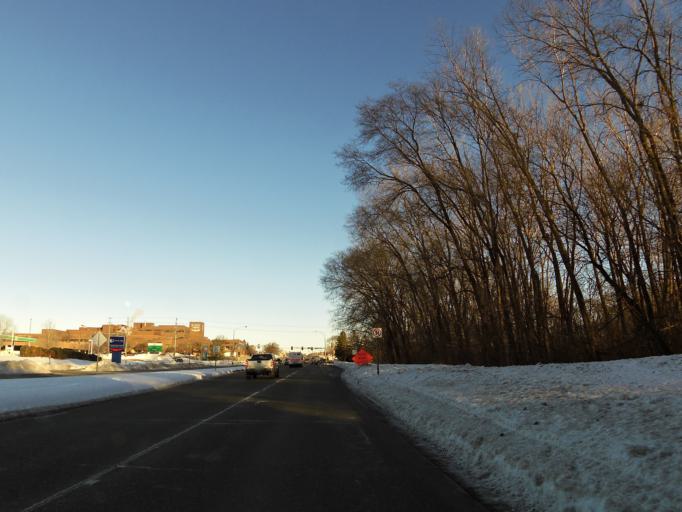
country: US
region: Minnesota
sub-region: Ramsey County
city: Vadnais Heights
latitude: 45.0280
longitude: -93.0380
